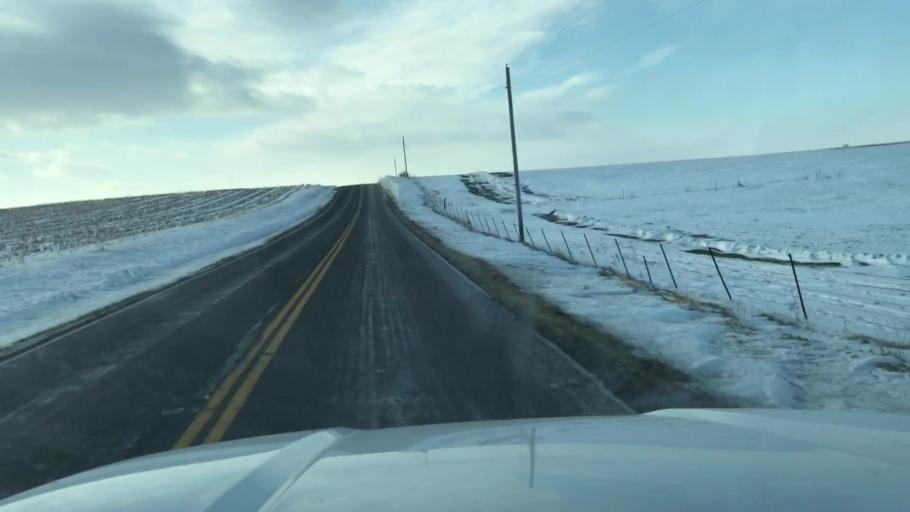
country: US
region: Missouri
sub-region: Nodaway County
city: Maryville
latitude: 40.2011
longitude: -94.9078
